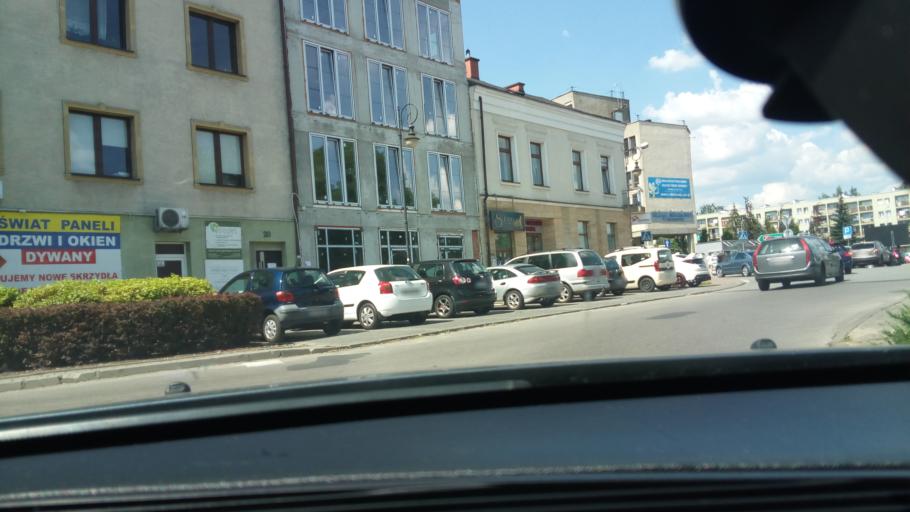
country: PL
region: Lesser Poland Voivodeship
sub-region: Powiat chrzanowski
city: Chrzanow
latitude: 50.1424
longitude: 19.4072
